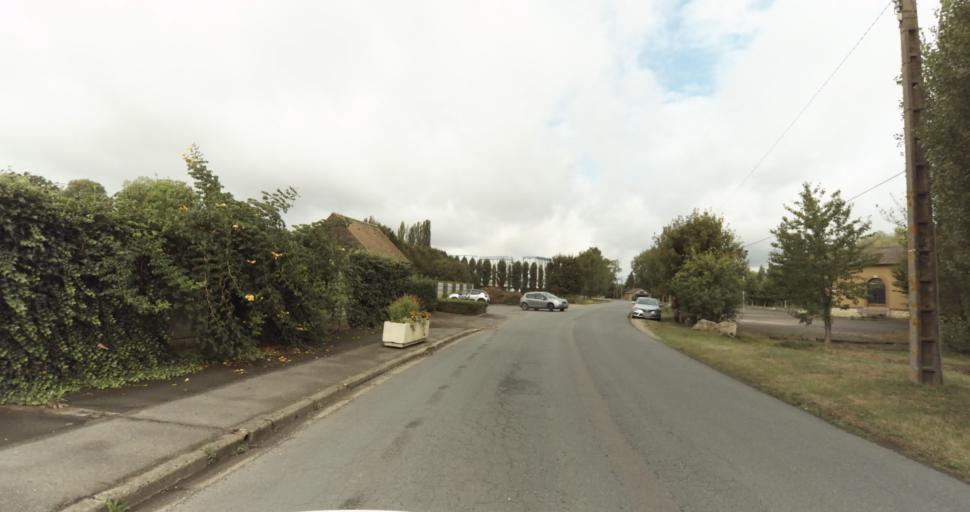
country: FR
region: Lower Normandy
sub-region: Departement de l'Orne
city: Vimoutiers
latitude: 48.9315
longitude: 0.1945
